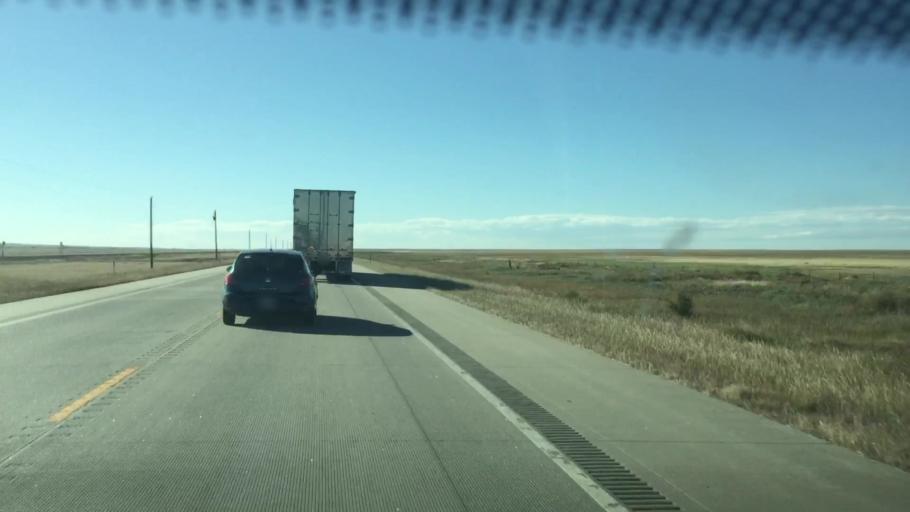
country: US
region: Colorado
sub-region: Kiowa County
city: Eads
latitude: 38.8305
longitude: -103.0406
